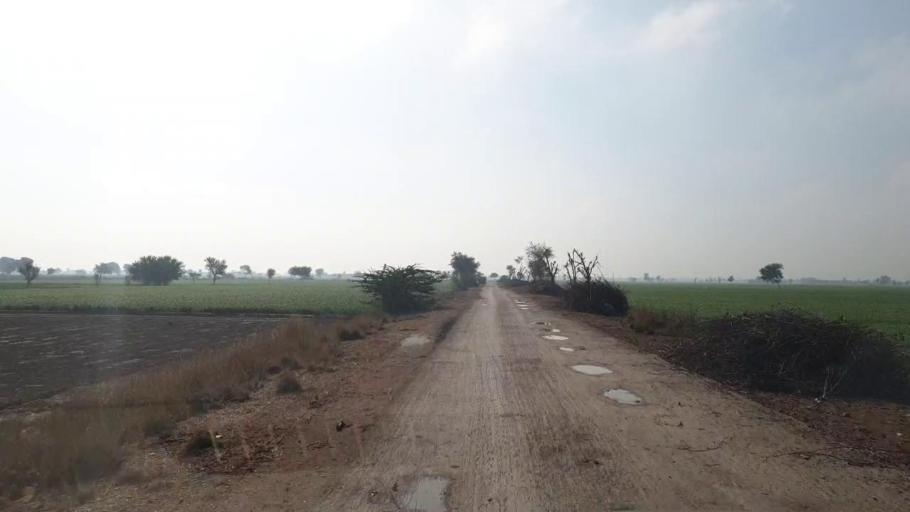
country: PK
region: Sindh
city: Shahdadpur
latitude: 26.0001
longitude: 68.6221
